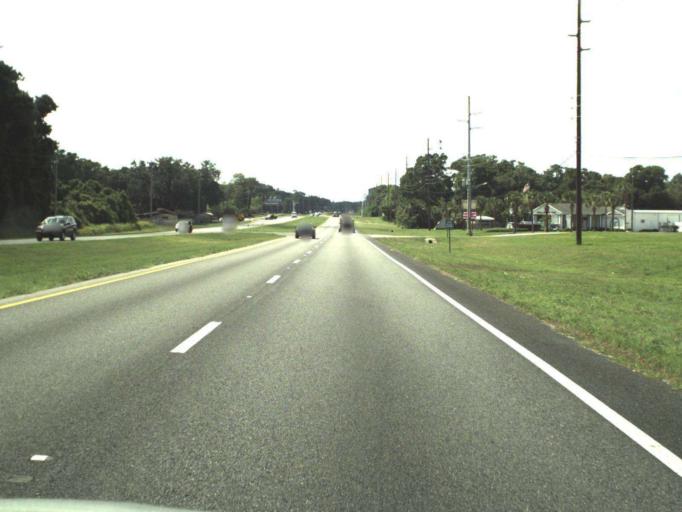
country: US
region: Florida
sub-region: Marion County
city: Ocala
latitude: 29.1514
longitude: -82.0765
